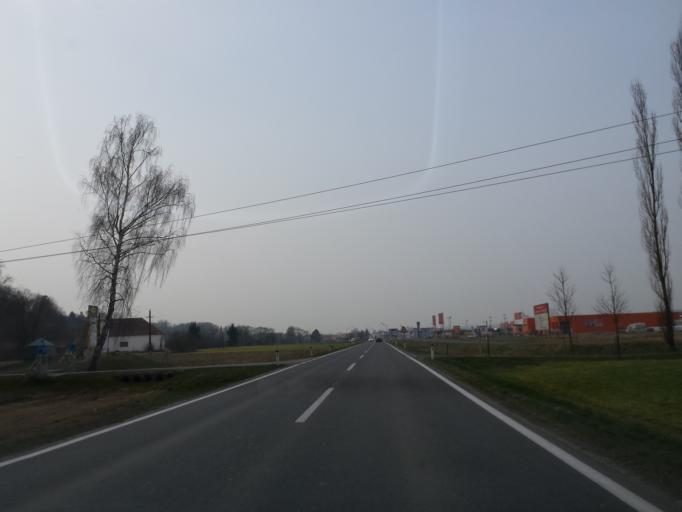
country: AT
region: Styria
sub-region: Politischer Bezirk Hartberg-Fuerstenfeld
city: Fuerstenfeld
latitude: 47.0508
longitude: 16.0847
